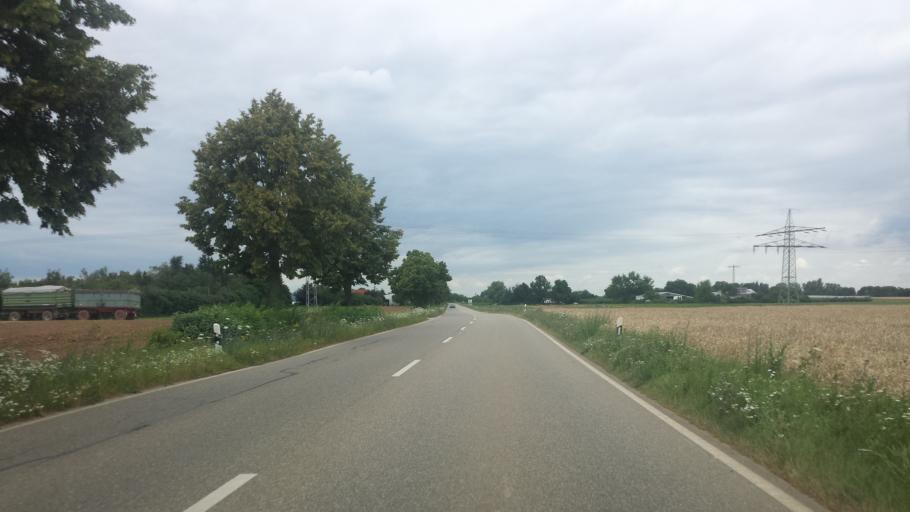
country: DE
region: Rheinland-Pfalz
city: Meckenheim
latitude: 49.3881
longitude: 8.2470
